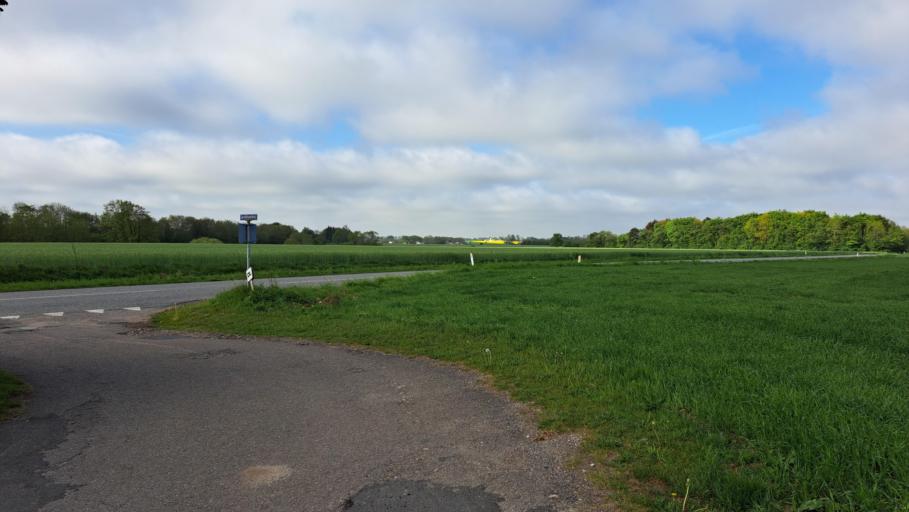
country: DK
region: Central Jutland
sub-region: Hedensted Kommune
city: Hedensted
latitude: 55.8019
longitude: 9.6651
